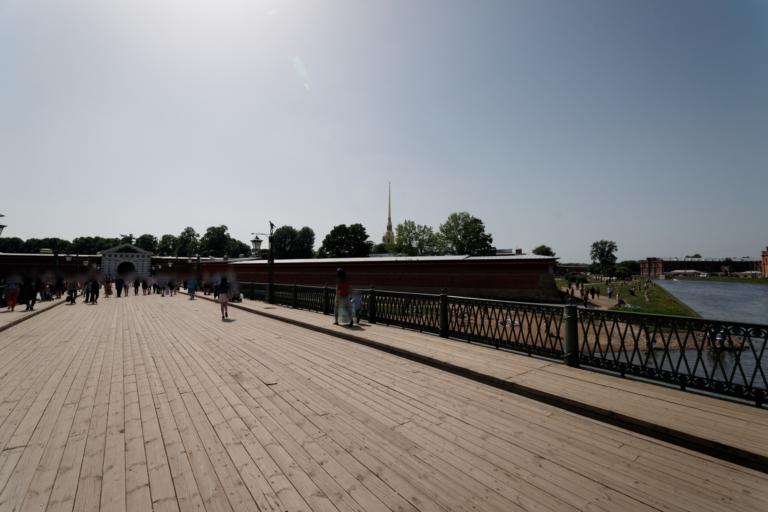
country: RU
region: St.-Petersburg
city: Saint Petersburg
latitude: 59.9522
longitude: 30.3225
